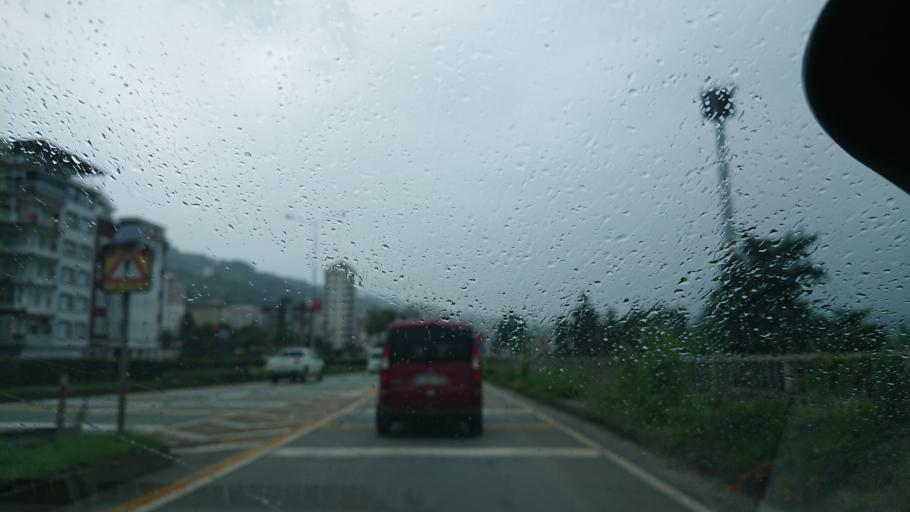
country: TR
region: Rize
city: Gundogdu
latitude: 41.0363
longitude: 40.5621
